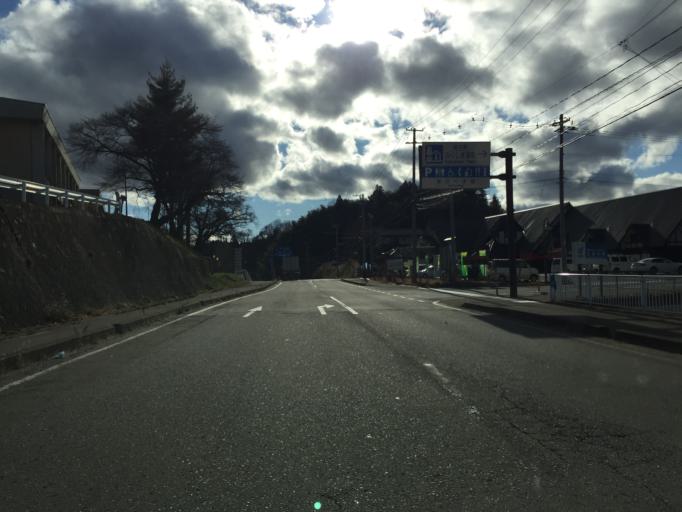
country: JP
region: Fukushima
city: Funehikimachi-funehiki
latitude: 37.5705
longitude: 140.5784
